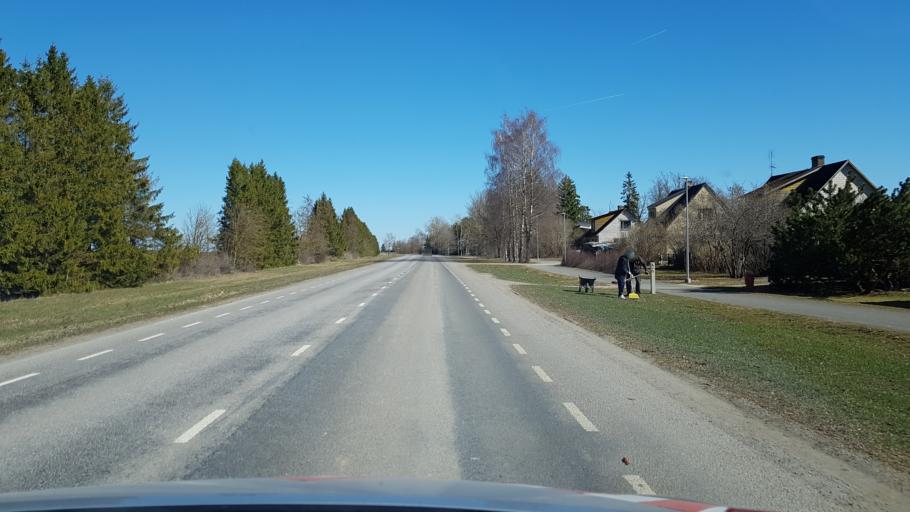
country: EE
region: Laeaene-Virumaa
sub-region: Someru vald
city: Someru
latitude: 59.3648
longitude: 26.4126
